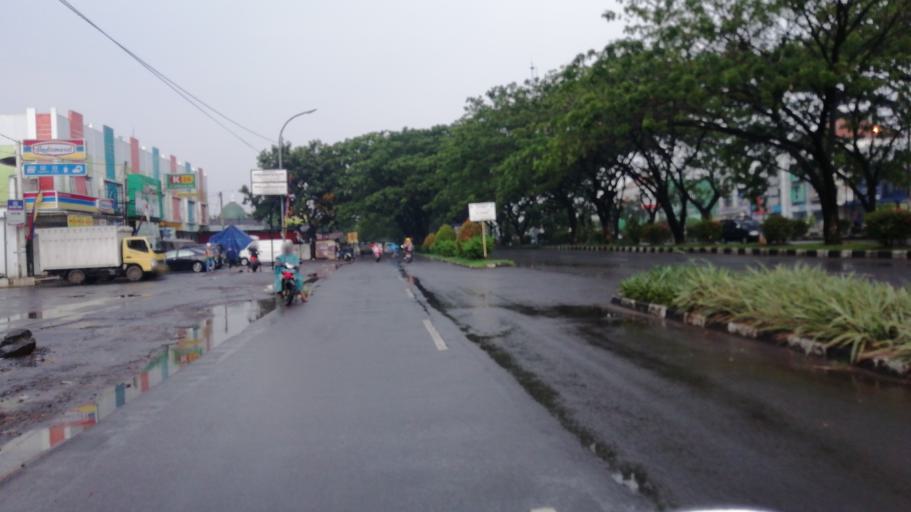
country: ID
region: West Java
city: Cibinong
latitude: -6.4818
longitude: 106.8107
